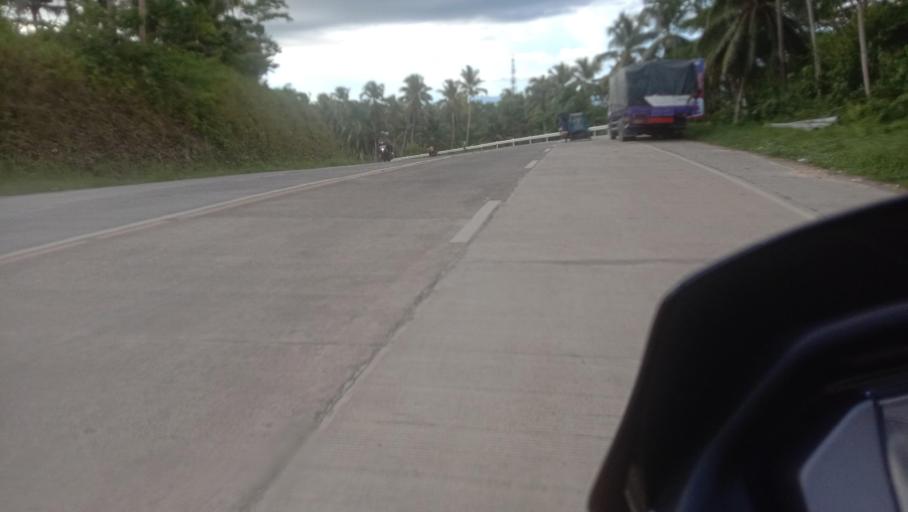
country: PH
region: Caraga
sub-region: Province of Surigao del Sur
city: Barobo
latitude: 8.5229
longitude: 126.1202
